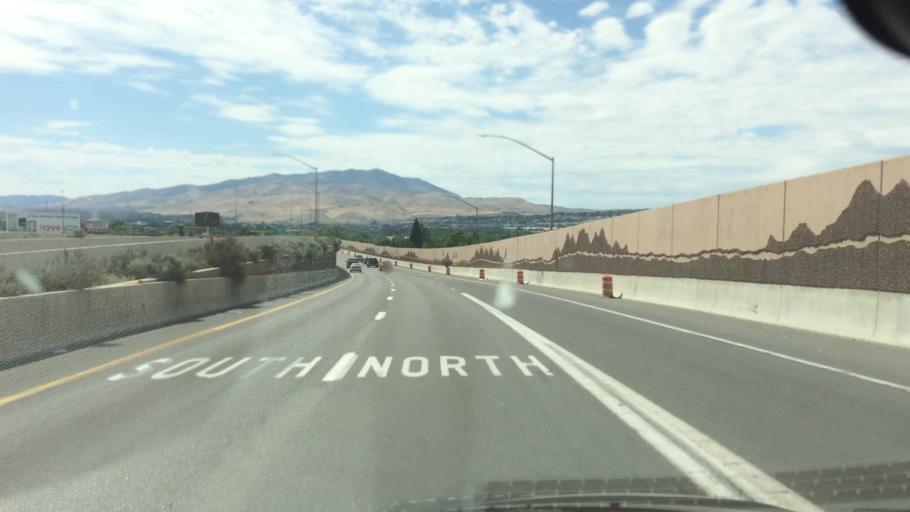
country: US
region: Nevada
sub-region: Washoe County
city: Sparks
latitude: 39.5364
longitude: -119.7800
